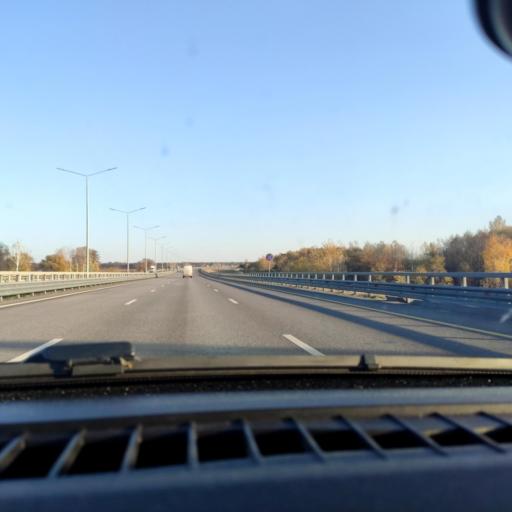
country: RU
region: Voronezj
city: Somovo
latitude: 51.7915
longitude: 39.2718
